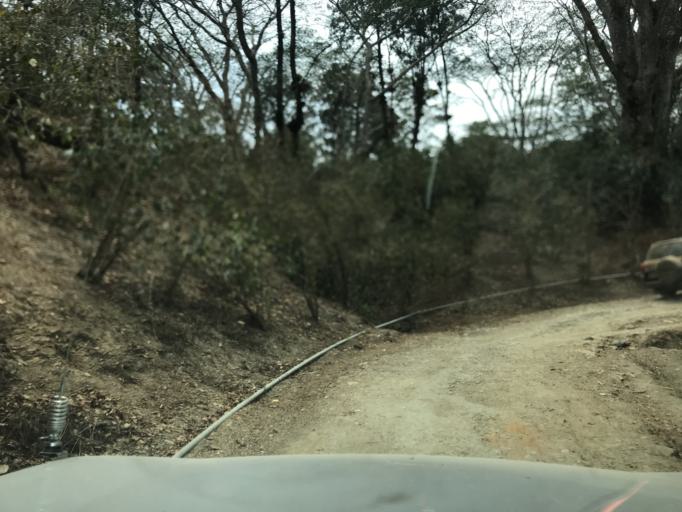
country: TL
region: Ermera
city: Gleno
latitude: -8.8362
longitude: 125.4476
